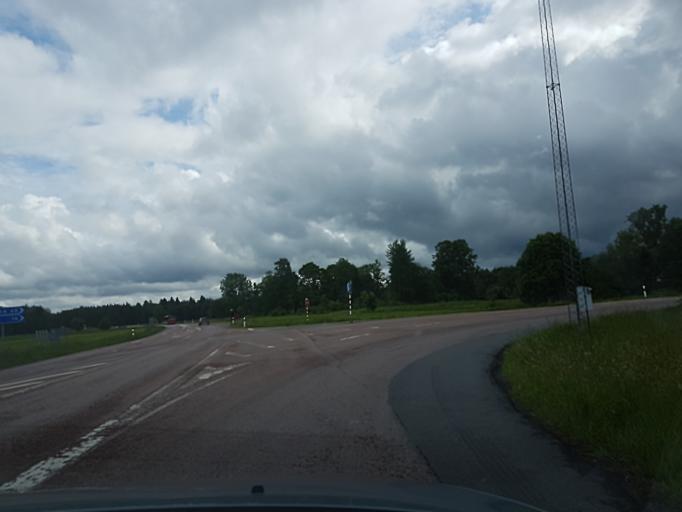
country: SE
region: Uppsala
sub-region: Osthammars Kommun
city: OEsthammar
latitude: 60.2437
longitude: 18.3486
